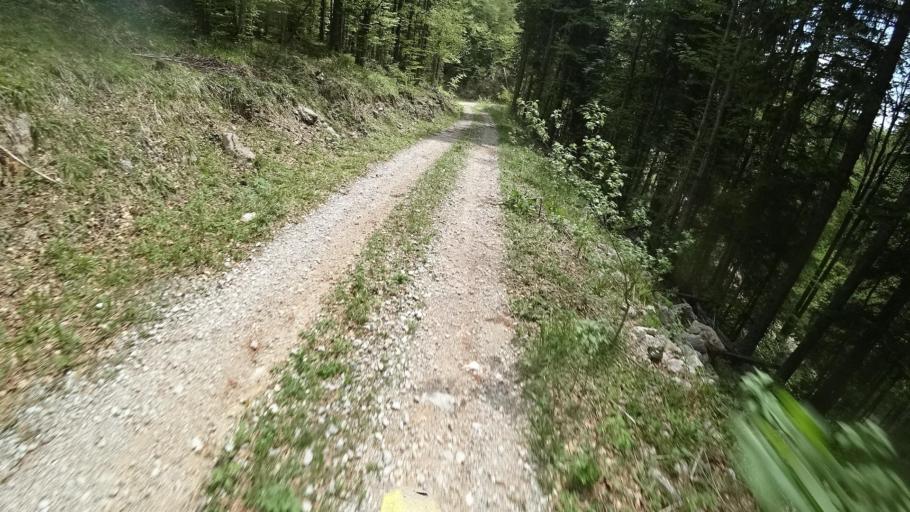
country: BA
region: Republika Srpska
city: Sipovo
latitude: 44.1472
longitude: 17.0541
